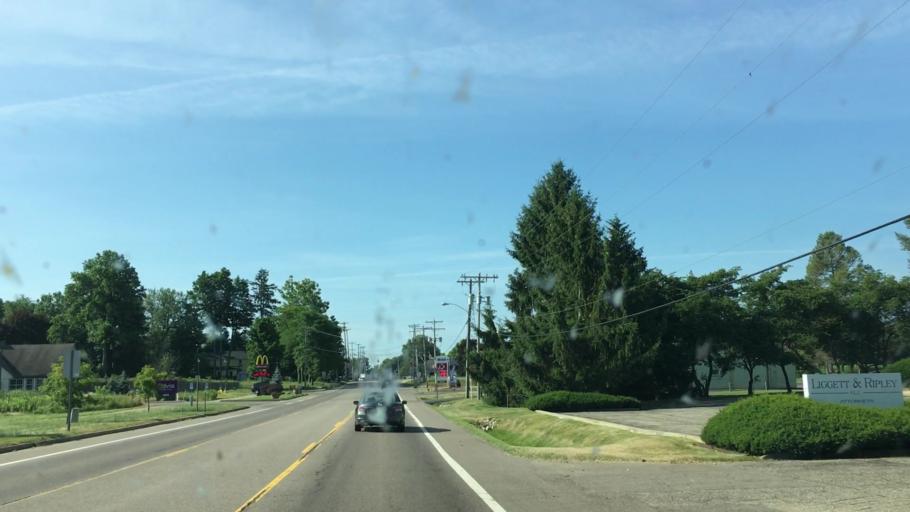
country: US
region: Michigan
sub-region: Kalamazoo County
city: South Gull Lake
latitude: 42.3806
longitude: -85.4553
